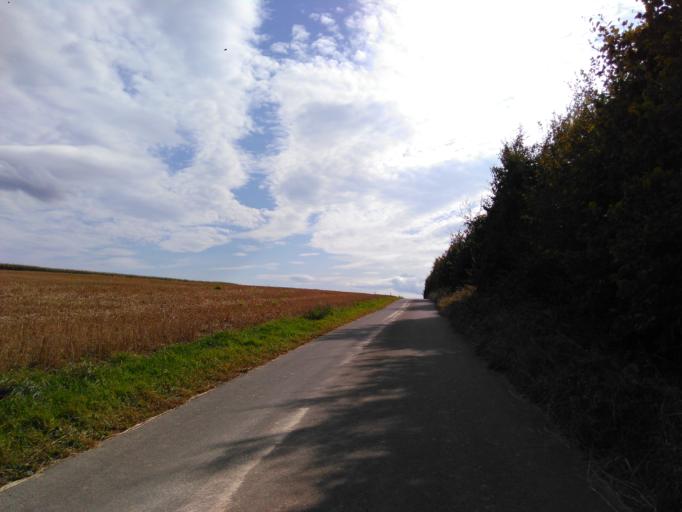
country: BE
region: Wallonia
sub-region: Province du Luxembourg
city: Gouvy
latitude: 50.1696
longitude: 5.9644
